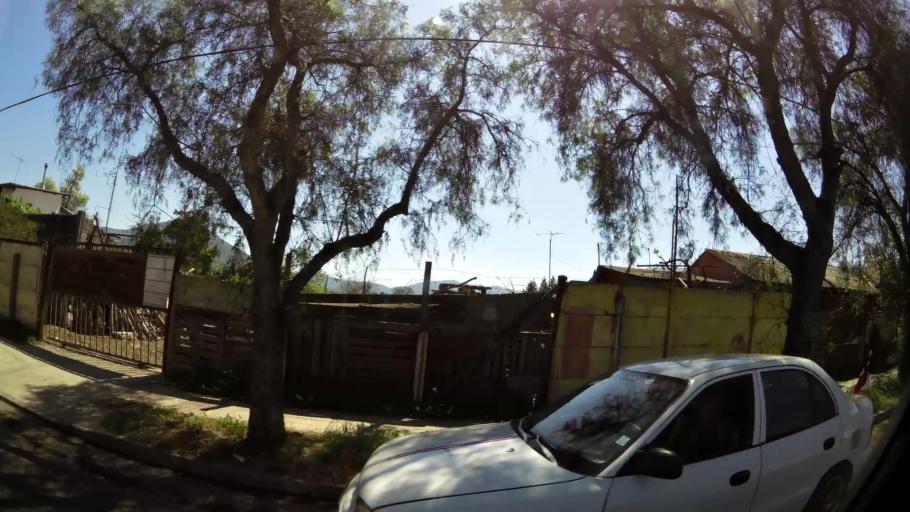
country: CL
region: Santiago Metropolitan
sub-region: Provincia de Talagante
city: Talagante
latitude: -33.6528
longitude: -70.9277
